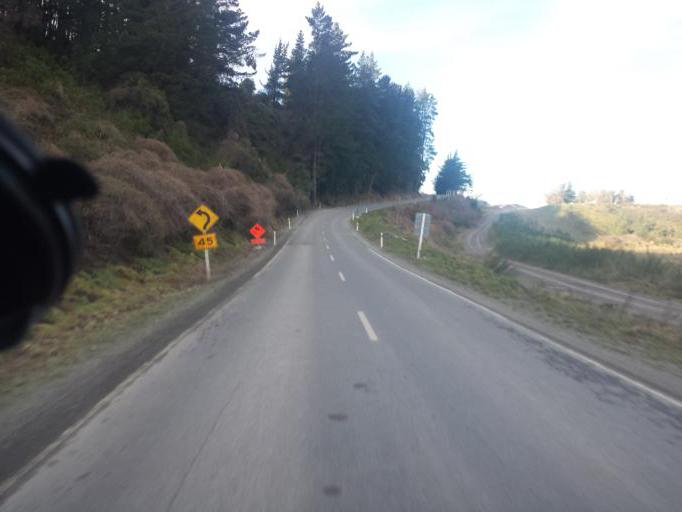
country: NZ
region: Canterbury
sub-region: Ashburton District
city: Methven
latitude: -43.5276
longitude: 171.6772
